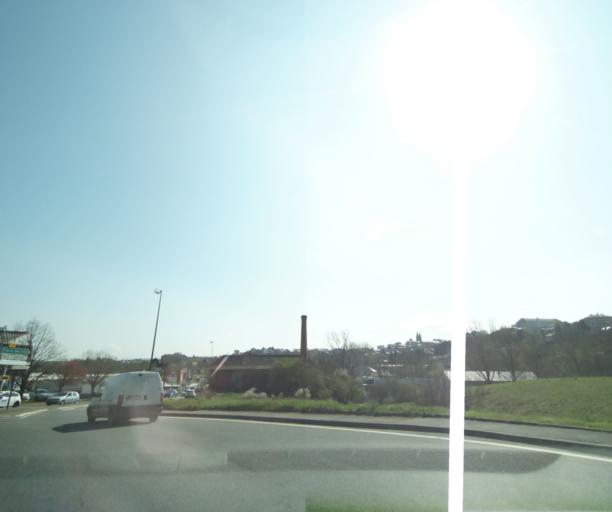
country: FR
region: Midi-Pyrenees
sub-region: Departement de l'Aveyron
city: Rodez
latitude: 44.3618
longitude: 2.5652
